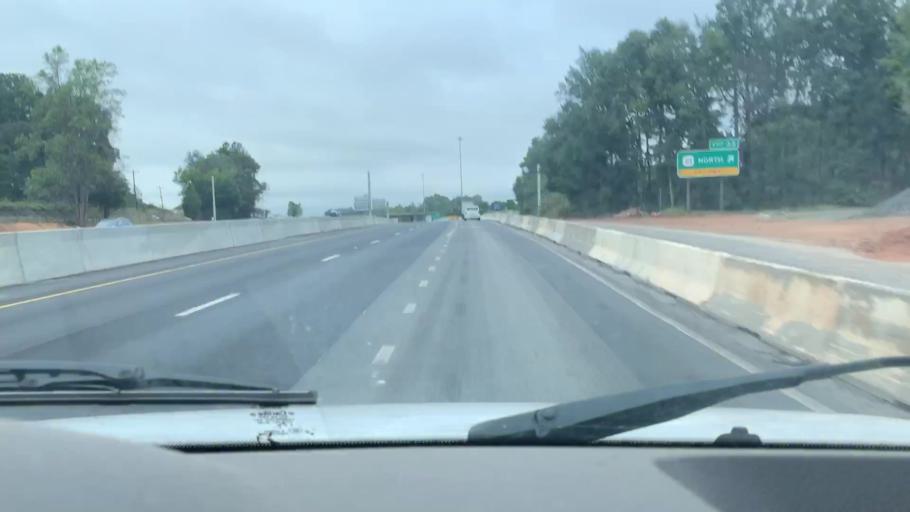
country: US
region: North Carolina
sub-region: Gaston County
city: Davidson
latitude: 35.5493
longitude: -80.8580
